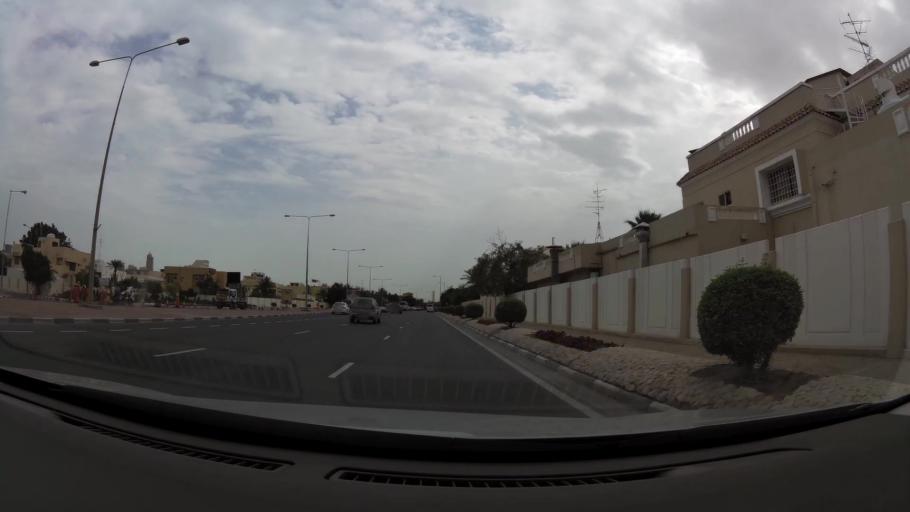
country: QA
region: Baladiyat ad Dawhah
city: Doha
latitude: 25.3326
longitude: 51.5059
